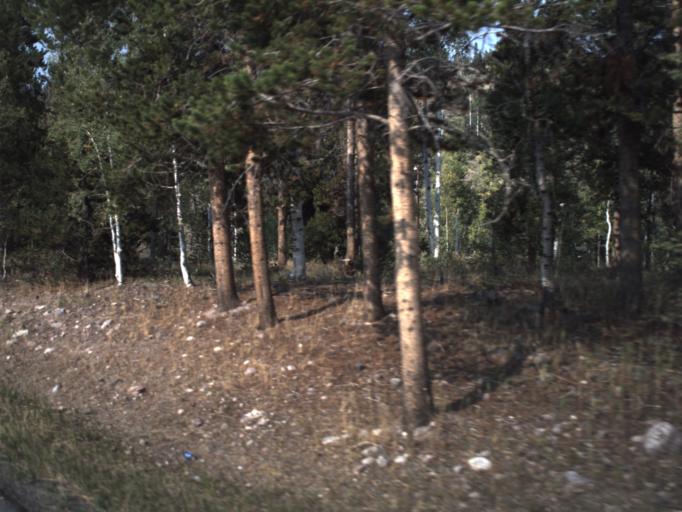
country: US
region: Wyoming
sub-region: Uinta County
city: Evanston
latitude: 40.9270
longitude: -110.8286
